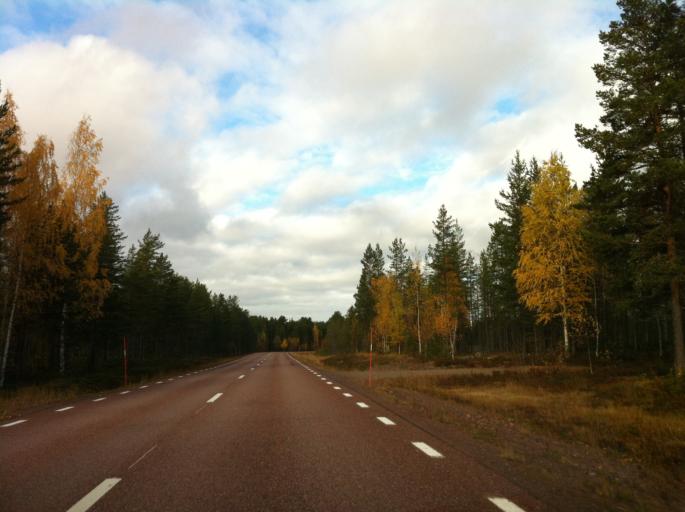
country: SE
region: Dalarna
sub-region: Alvdalens Kommun
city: AElvdalen
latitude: 61.5249
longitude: 13.3620
